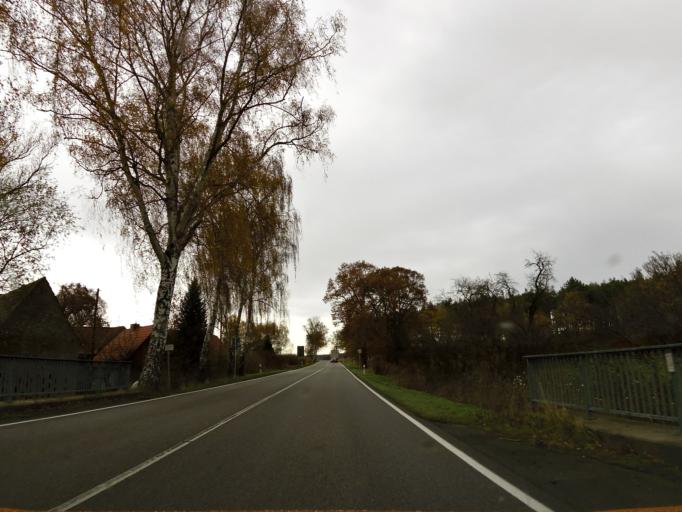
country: DE
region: Saxony-Anhalt
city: Kalbe
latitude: 52.6043
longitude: 11.3245
